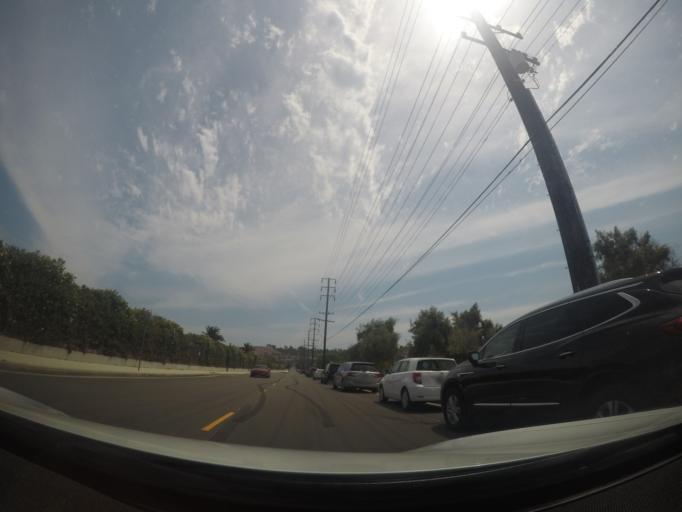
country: US
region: California
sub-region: Los Angeles County
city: Rolling Hills Estates
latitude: 33.8121
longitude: -118.3544
